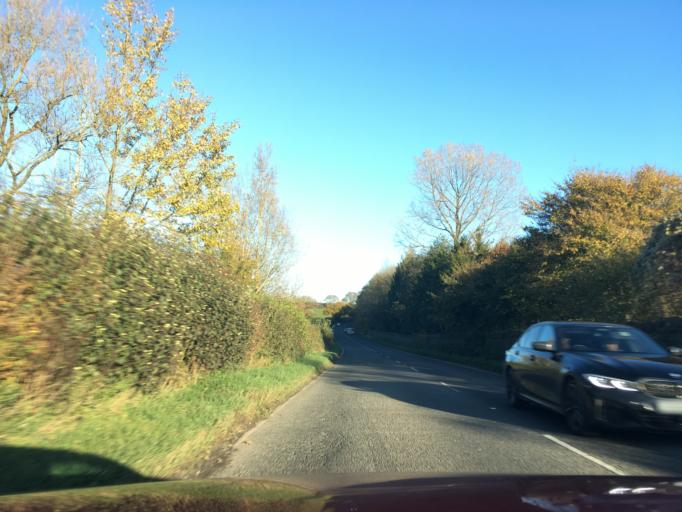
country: GB
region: England
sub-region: Somerset
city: Milborne Port
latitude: 50.9626
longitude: -2.4830
